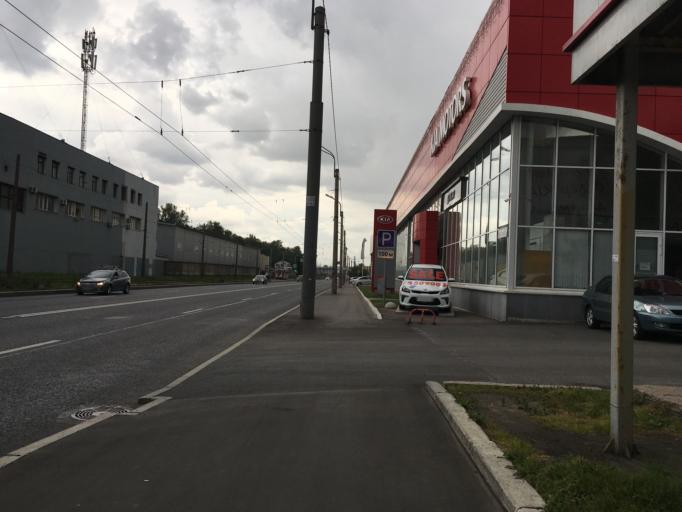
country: RU
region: St.-Petersburg
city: Centralniy
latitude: 59.9031
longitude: 30.3540
